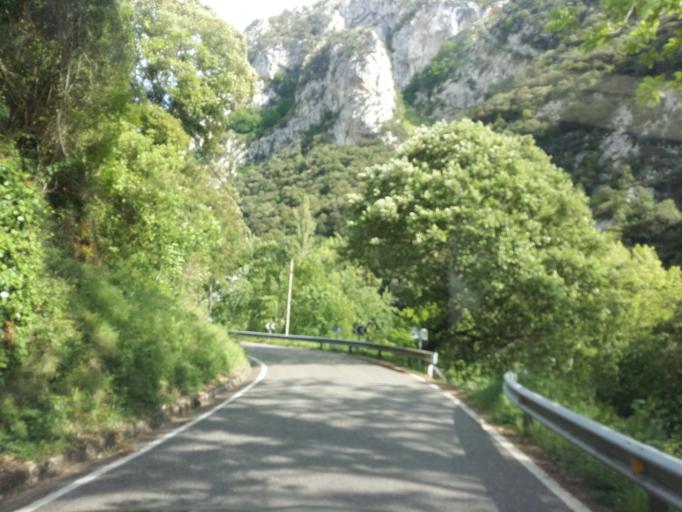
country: ES
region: Cantabria
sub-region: Provincia de Cantabria
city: Tresviso
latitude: 43.2535
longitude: -4.6121
